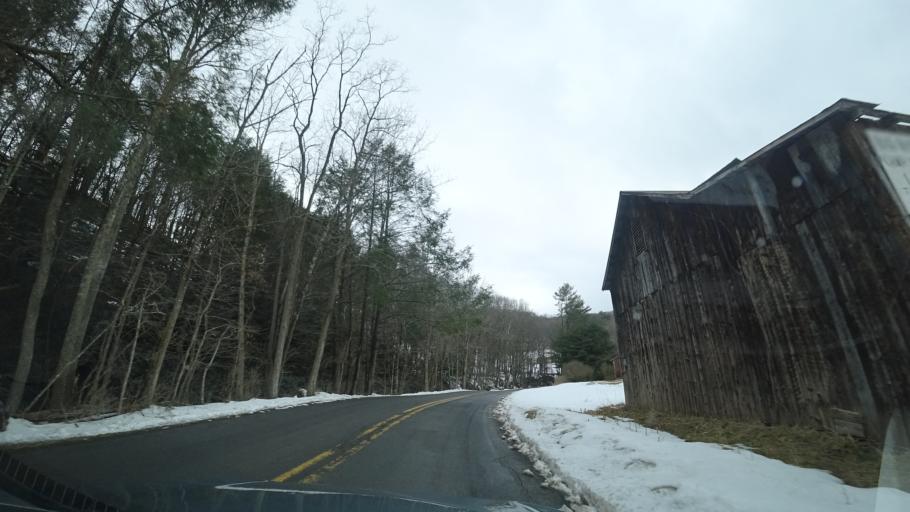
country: US
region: Virginia
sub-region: Shenandoah County
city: Basye
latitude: 38.8885
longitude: -78.8962
